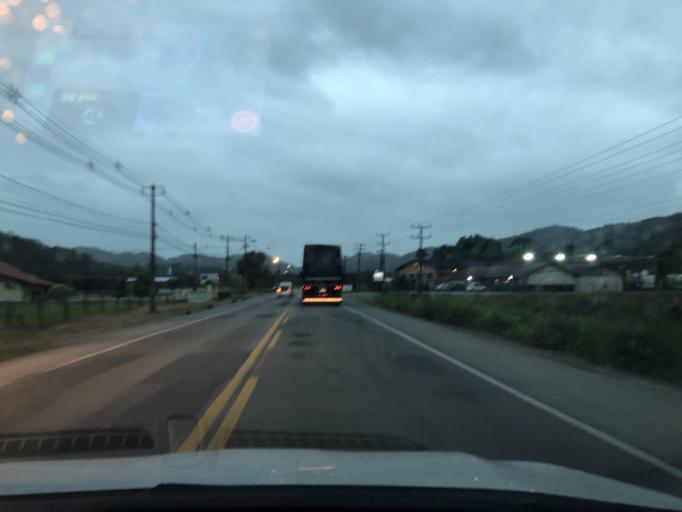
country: BR
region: Santa Catarina
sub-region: Pomerode
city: Pomerode
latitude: -26.7791
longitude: -49.0832
